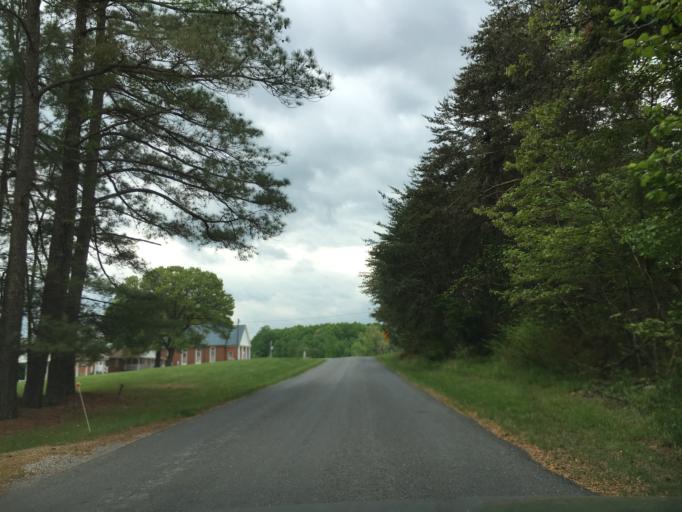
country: US
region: Virginia
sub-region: Campbell County
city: Rustburg
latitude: 37.2018
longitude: -79.0449
